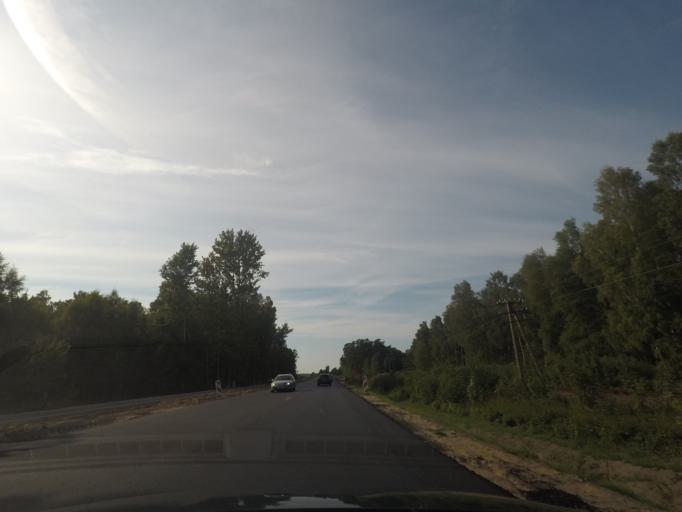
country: PL
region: Pomeranian Voivodeship
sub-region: Powiat leborski
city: Leba
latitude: 54.7321
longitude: 17.5635
